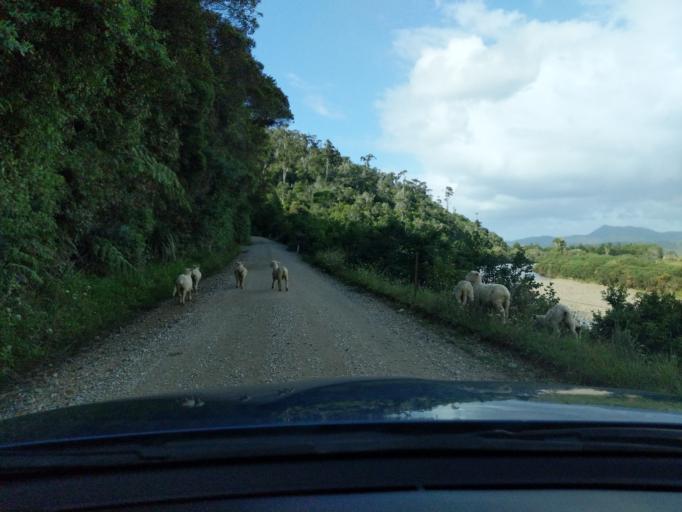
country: NZ
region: Tasman
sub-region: Tasman District
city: Takaka
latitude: -40.6535
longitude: 172.4582
